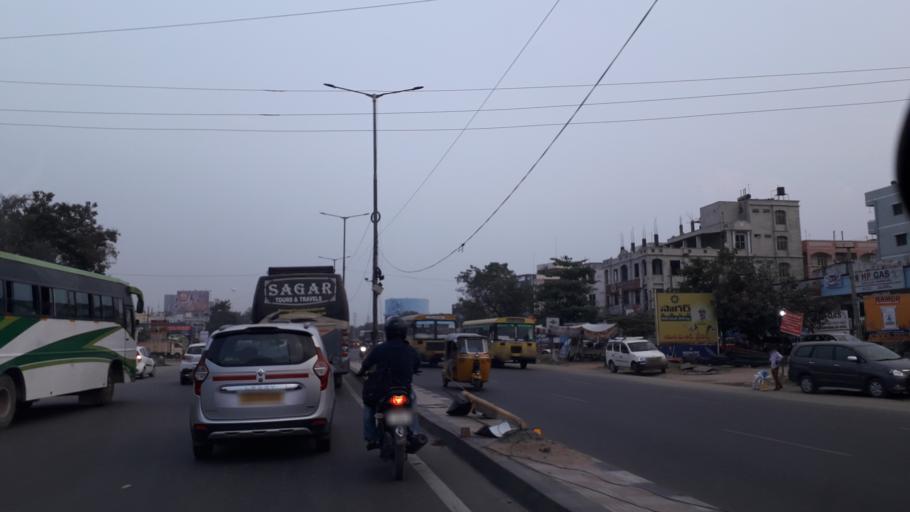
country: IN
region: Telangana
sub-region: Medak
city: Serilingampalle
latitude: 17.5088
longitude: 78.3009
